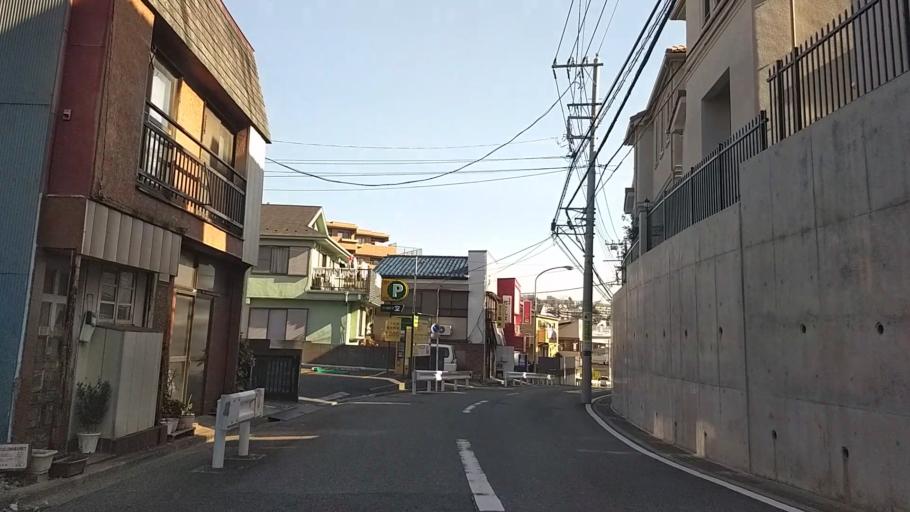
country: JP
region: Kanagawa
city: Yokohama
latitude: 35.3905
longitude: 139.5978
